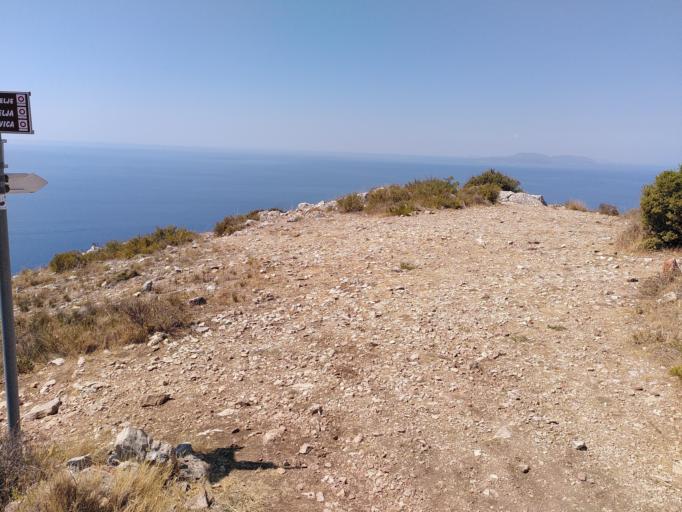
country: HR
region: Splitsko-Dalmatinska
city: Stari Grad
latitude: 43.1463
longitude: 16.5826
